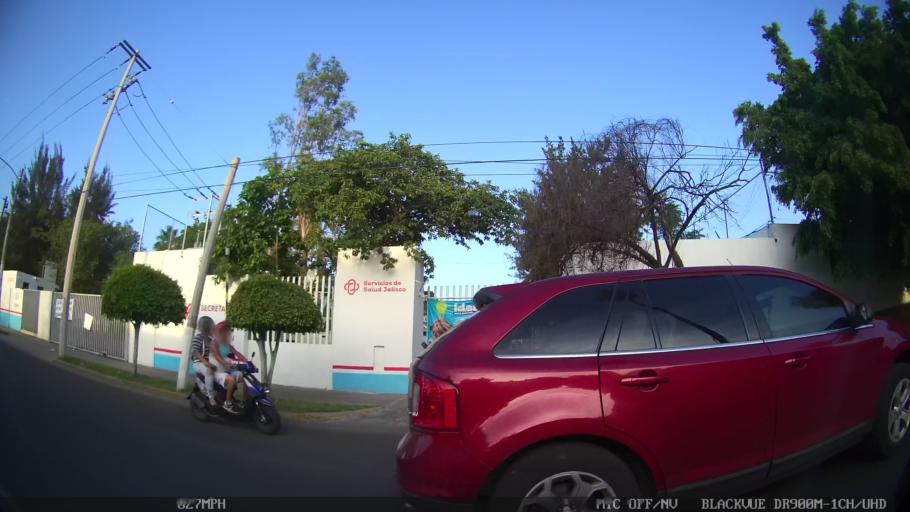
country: MX
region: Jalisco
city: Tlaquepaque
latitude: 20.6717
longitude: -103.3140
